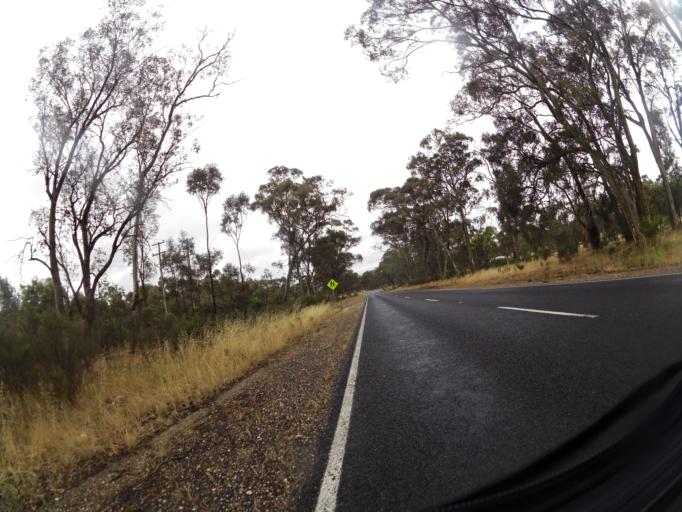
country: AU
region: Victoria
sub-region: Mount Alexander
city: Castlemaine
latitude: -37.0826
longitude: 144.1579
